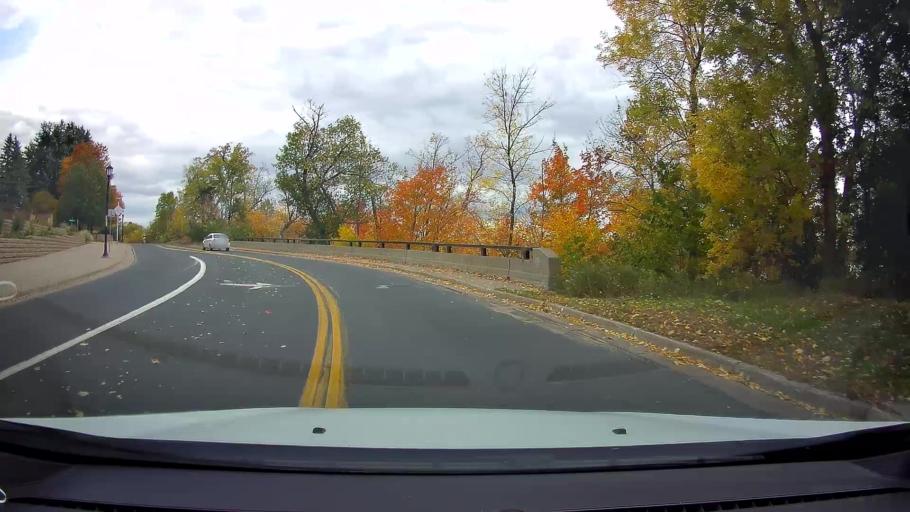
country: US
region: Minnesota
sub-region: Chisago County
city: Center City
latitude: 45.3966
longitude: -92.8187
